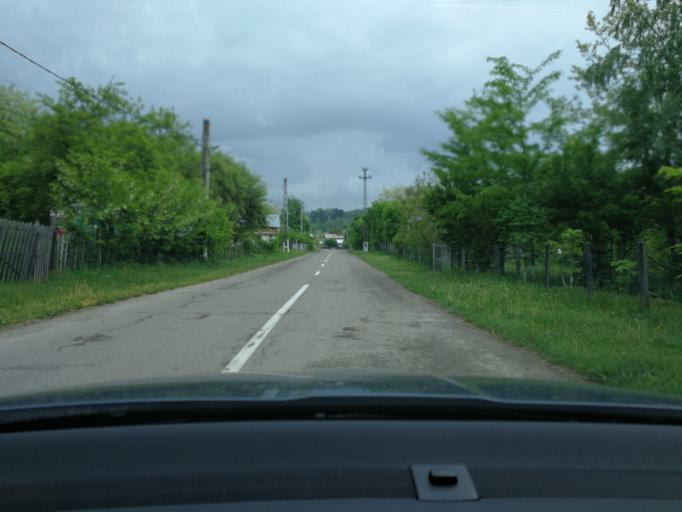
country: RO
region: Prahova
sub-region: Comuna Alunis
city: Alunis
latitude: 45.2056
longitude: 25.8451
